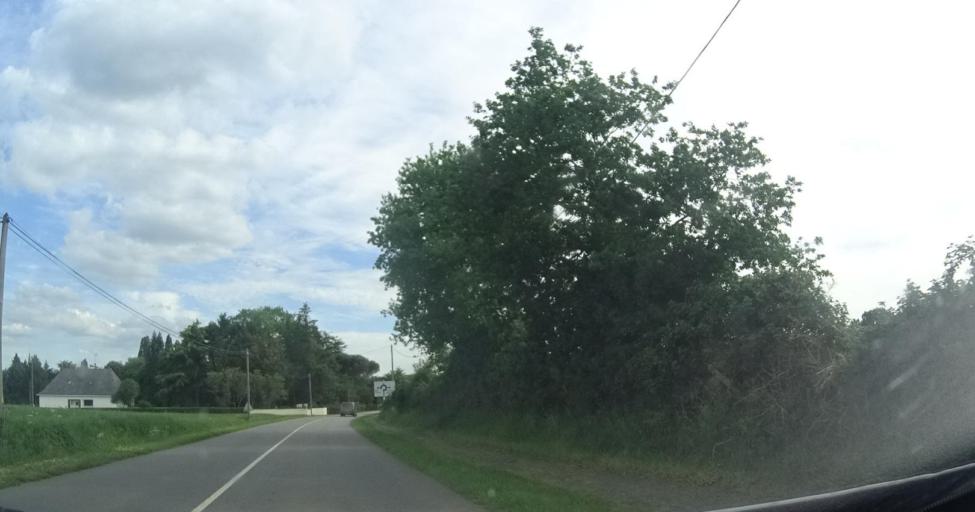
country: FR
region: Pays de la Loire
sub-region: Departement de la Loire-Atlantique
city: Fay-de-Bretagne
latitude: 47.4188
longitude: -1.7962
